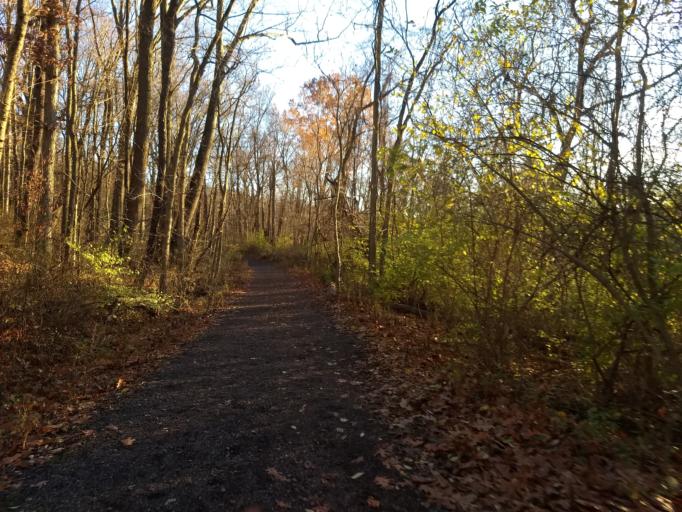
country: US
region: Pennsylvania
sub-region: Allegheny County
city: South Park Township
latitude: 40.2979
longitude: -80.0005
